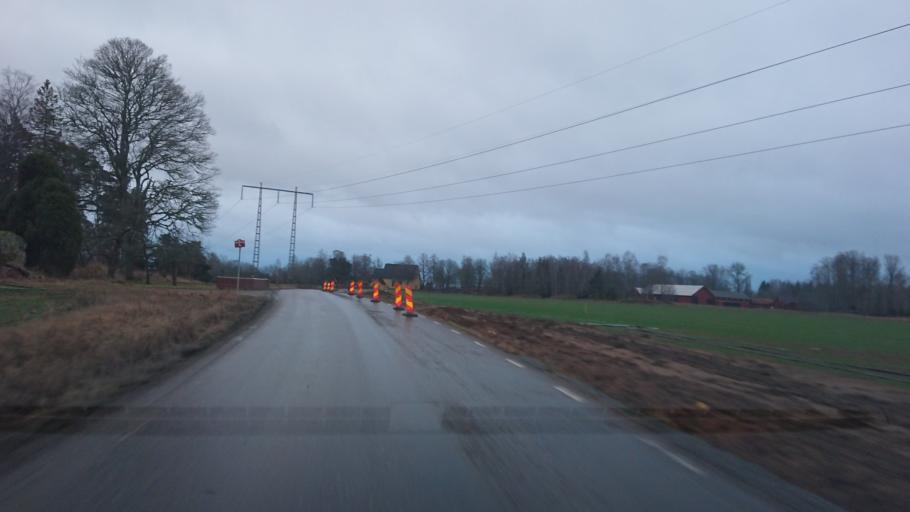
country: SE
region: Uppsala
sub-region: Uppsala Kommun
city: Gamla Uppsala
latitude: 59.9594
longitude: 17.6049
